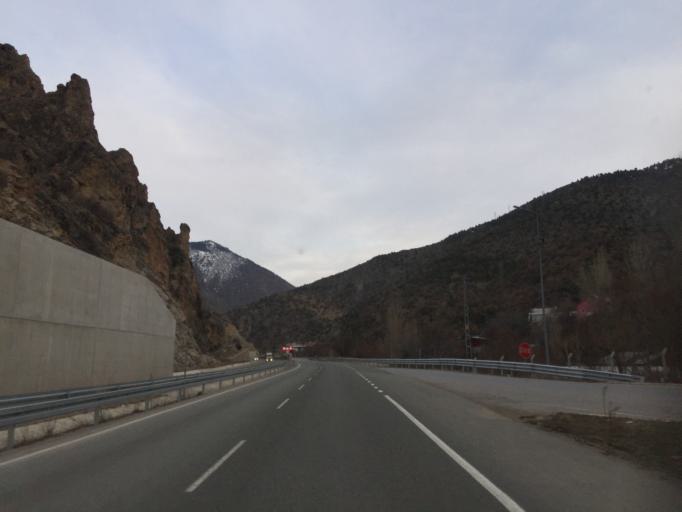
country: TR
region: Gumushane
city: Gumushkhane
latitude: 40.5219
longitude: 39.4024
